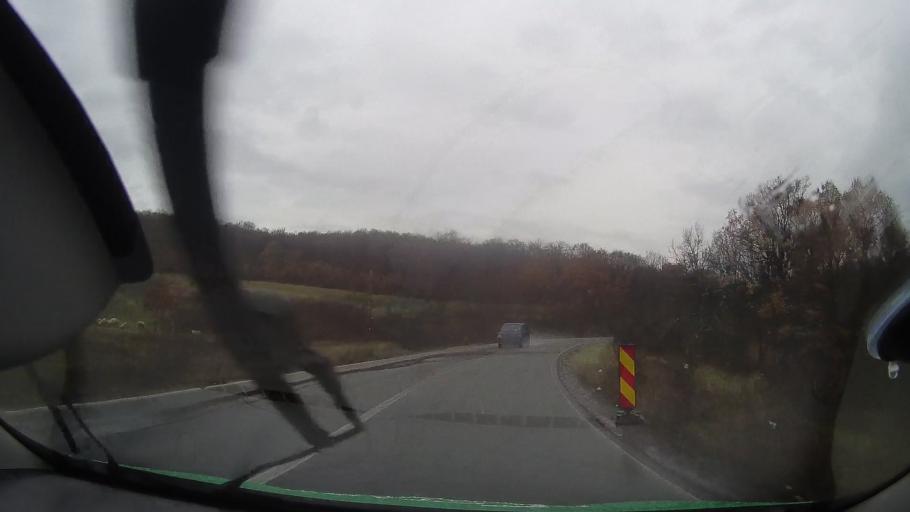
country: RO
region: Bihor
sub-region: Comuna Rabagani
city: Rabagani
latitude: 46.7323
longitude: 22.2311
